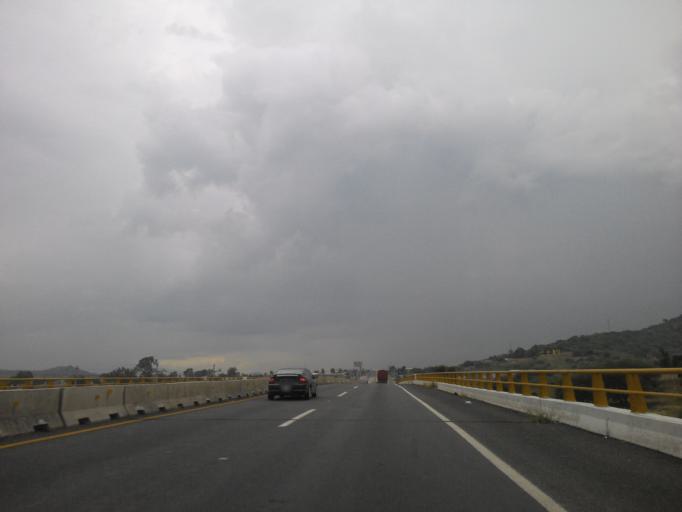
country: MX
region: Jalisco
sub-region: Tonala
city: Paseo Puente Viejo
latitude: 20.5733
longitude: -103.1886
